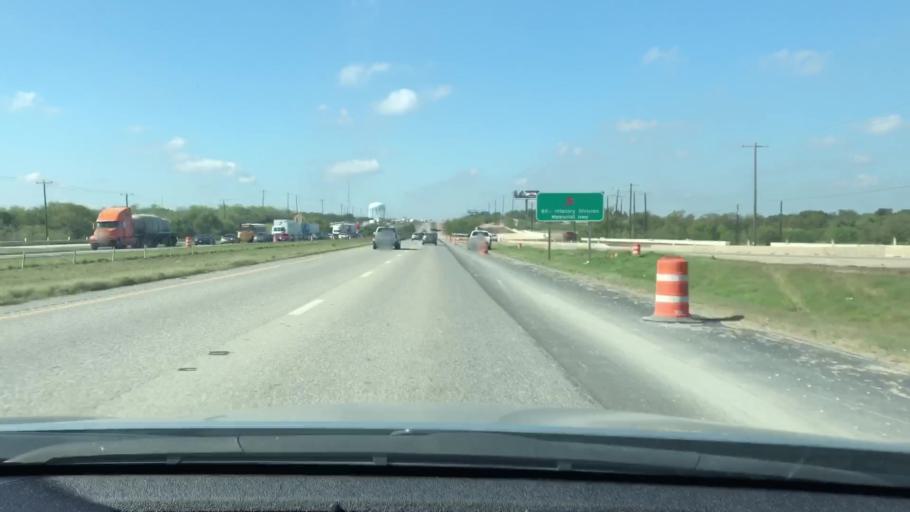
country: US
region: Texas
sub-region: Bexar County
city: Kirby
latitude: 29.4562
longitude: -98.3262
